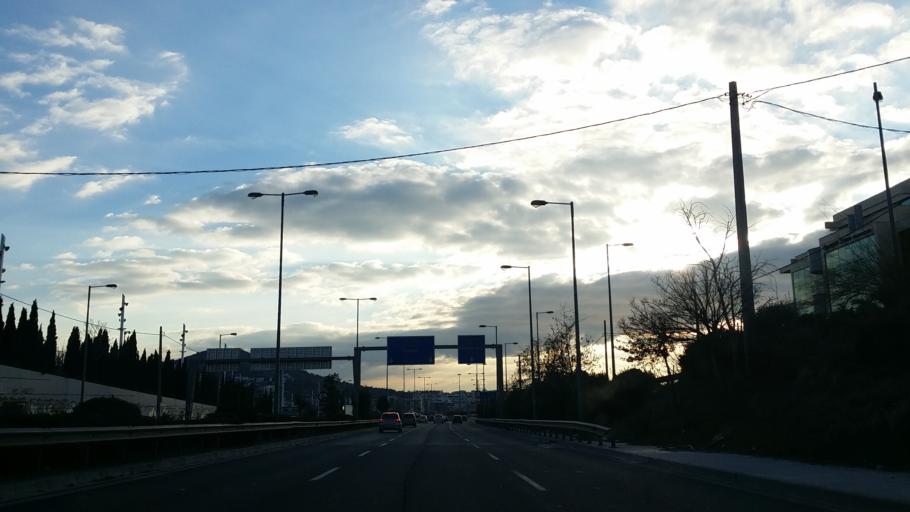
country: GR
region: Attica
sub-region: Nomarchia Athinas
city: Irakleio
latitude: 38.0438
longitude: 23.7803
